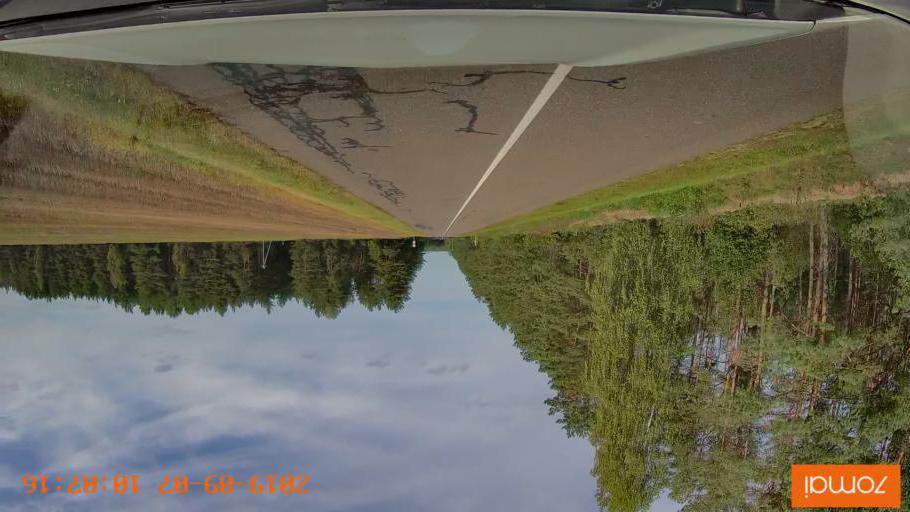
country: BY
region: Grodnenskaya
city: Voranava
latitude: 54.0733
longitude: 25.3968
